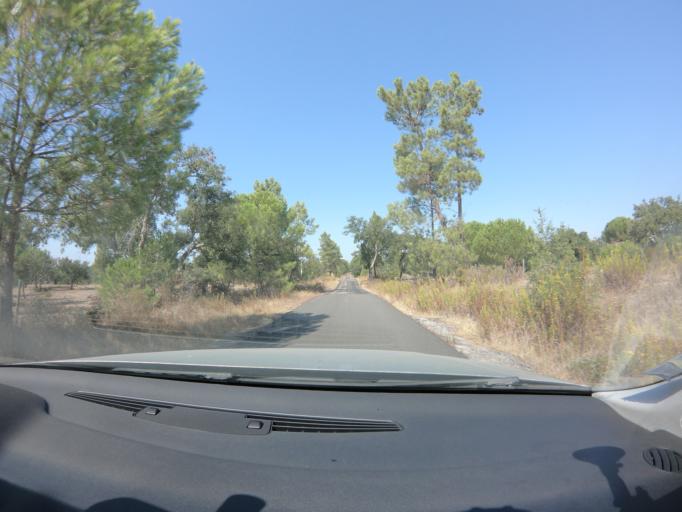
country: PT
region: Setubal
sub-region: Alcacer do Sal
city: Alcacer do Sal
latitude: 38.2641
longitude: -8.3130
